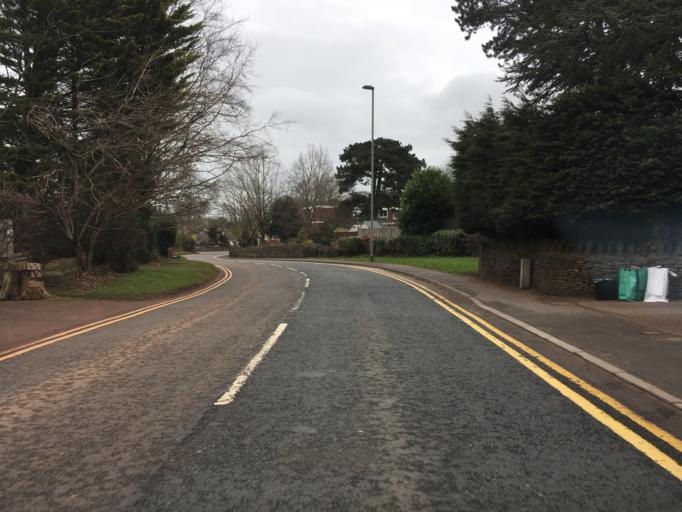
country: GB
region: England
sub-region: South Gloucestershire
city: Stoke Gifford
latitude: 51.5011
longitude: -2.5236
